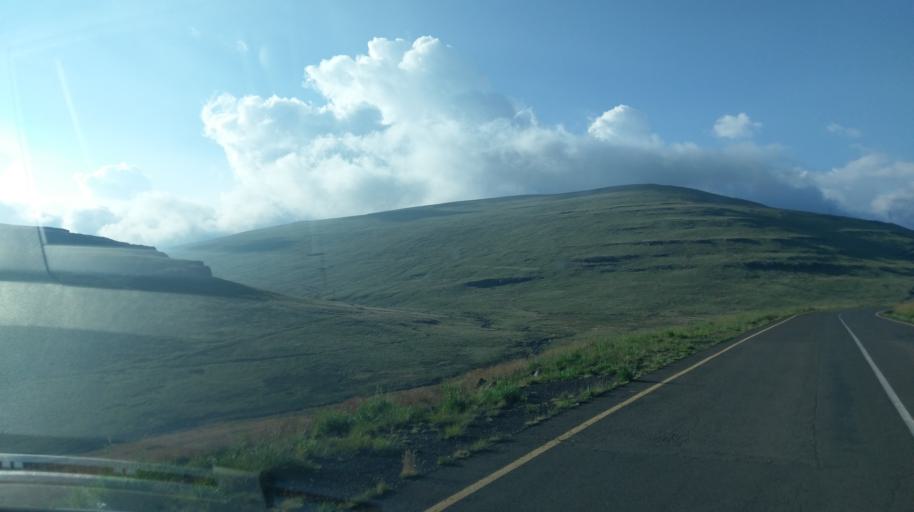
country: LS
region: Butha-Buthe
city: Butha-Buthe
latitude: -29.0854
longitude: 28.4256
